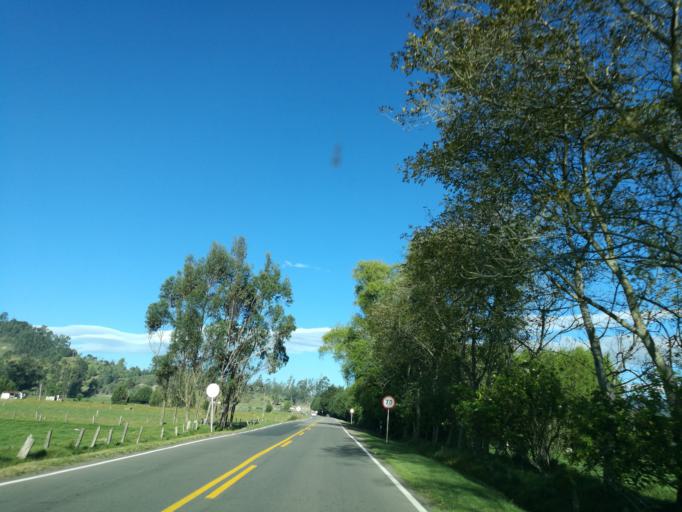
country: CO
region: Boyaca
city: Chiquinquira
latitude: 5.6236
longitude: -73.7649
